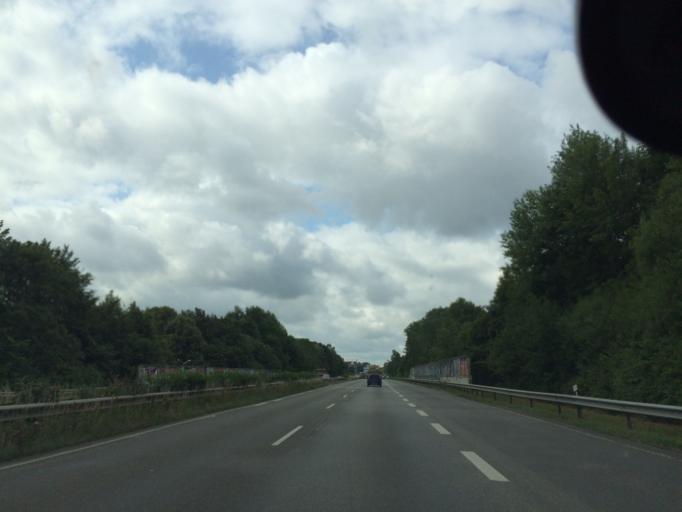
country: DE
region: Schleswig-Holstein
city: Kiel
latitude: 54.3420
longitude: 10.1162
